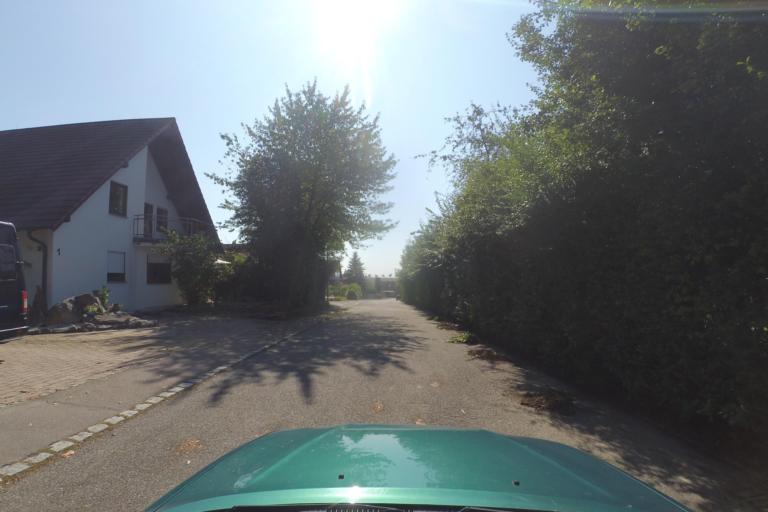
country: DE
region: Baden-Wuerttemberg
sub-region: Regierungsbezirk Stuttgart
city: Wolpertshausen
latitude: 49.1678
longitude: 9.8485
